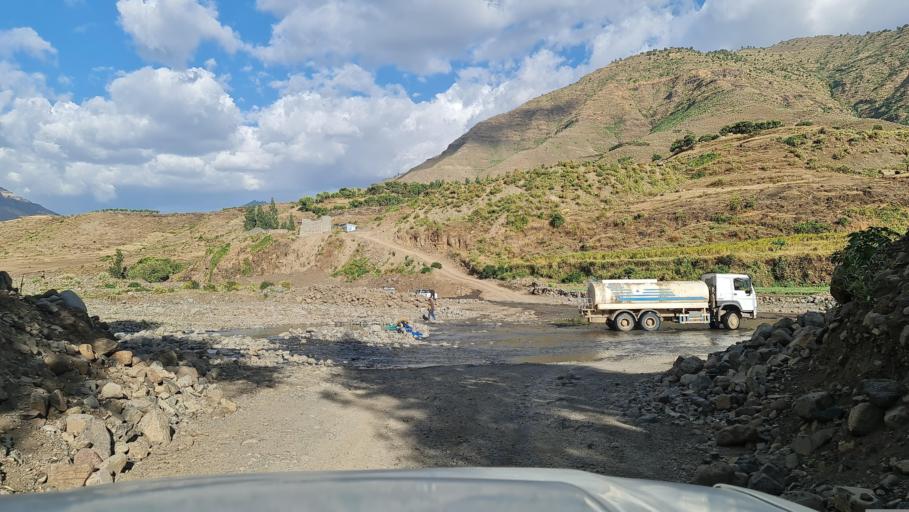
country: ET
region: Amhara
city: Debark'
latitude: 13.0820
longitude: 38.0116
